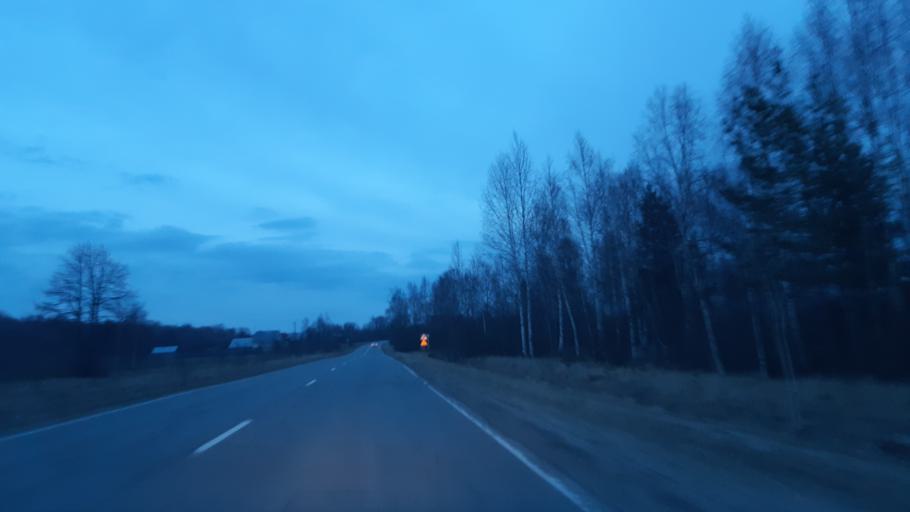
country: RU
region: Vladimir
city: Luknovo
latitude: 56.1842
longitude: 42.0155
